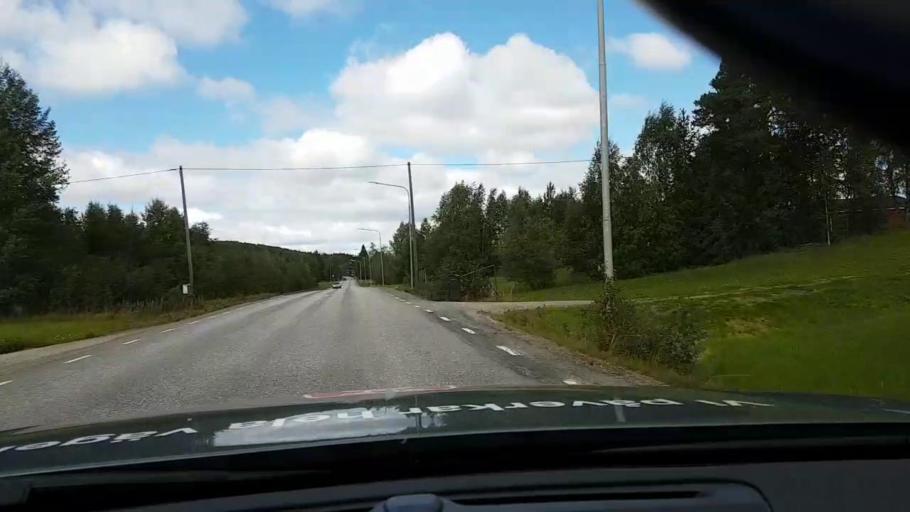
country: SE
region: Vaesternorrland
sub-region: OErnskoeldsviks Kommun
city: Bredbyn
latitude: 63.4821
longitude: 18.0899
